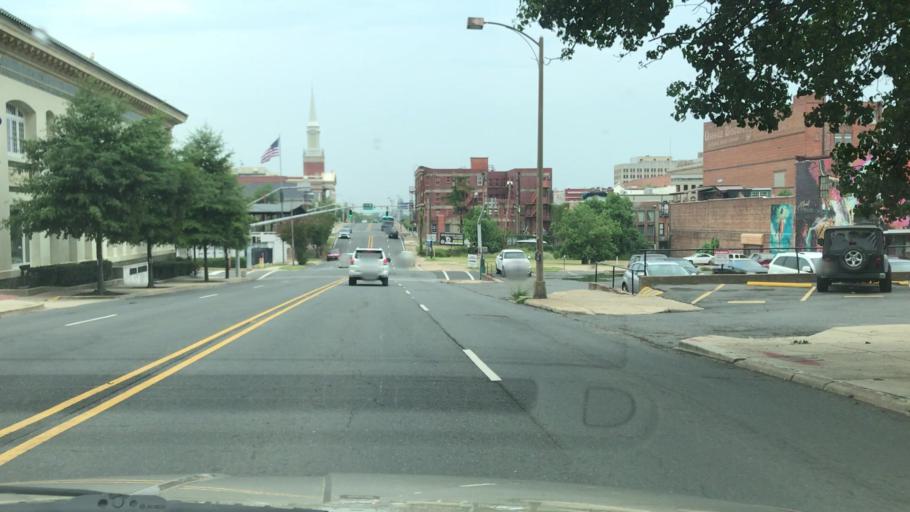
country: US
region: Louisiana
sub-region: Caddo Parish
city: Shreveport
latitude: 32.5087
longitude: -93.7504
